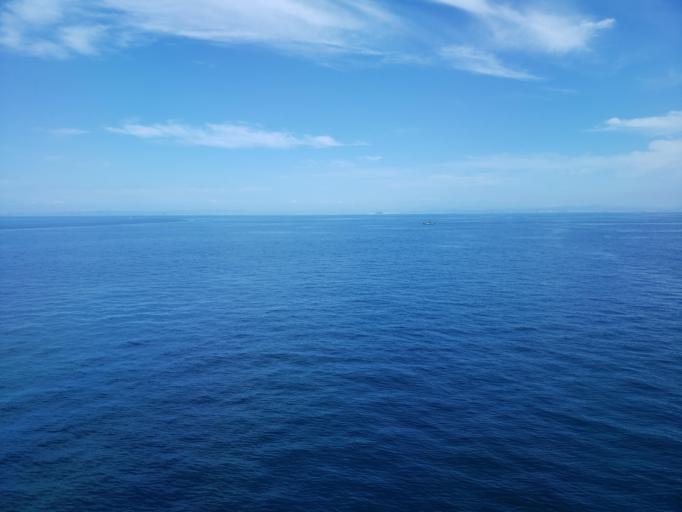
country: JP
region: Hyogo
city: Kakogawacho-honmachi
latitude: 34.5561
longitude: 134.7543
